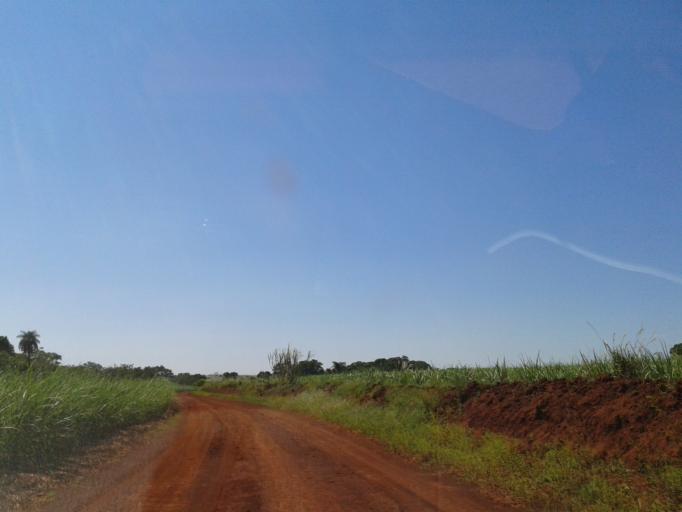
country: BR
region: Minas Gerais
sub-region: Centralina
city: Centralina
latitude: -18.6352
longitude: -49.2588
